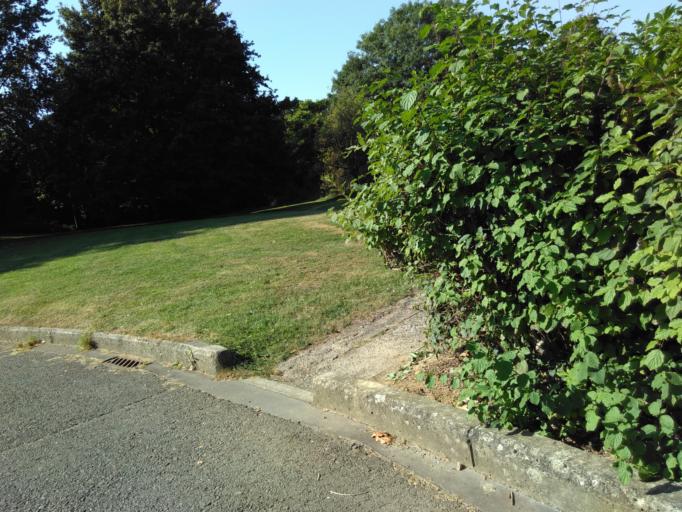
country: BE
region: Brussels Capital
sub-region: Bruxelles-Capitale
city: Brussels
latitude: 50.8205
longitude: 4.3959
